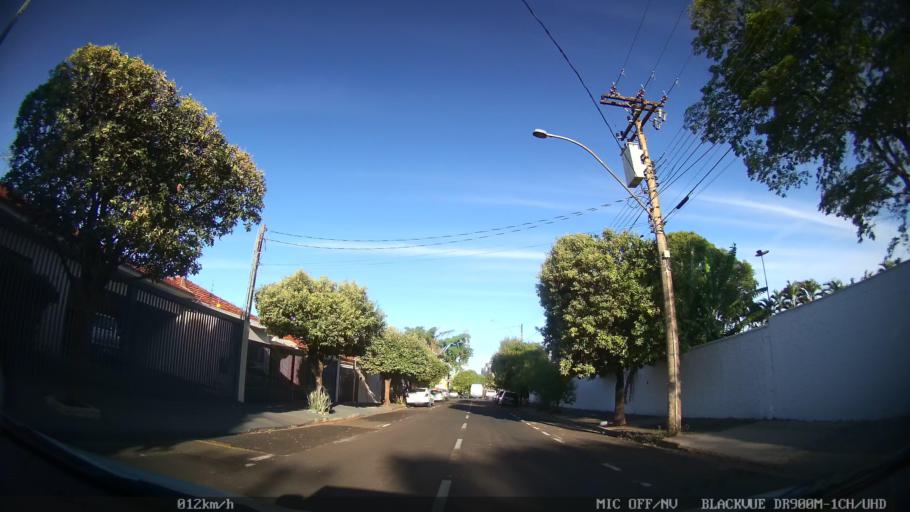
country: BR
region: Sao Paulo
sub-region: Sao Jose Do Rio Preto
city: Sao Jose do Rio Preto
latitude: -20.8326
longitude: -49.3725
